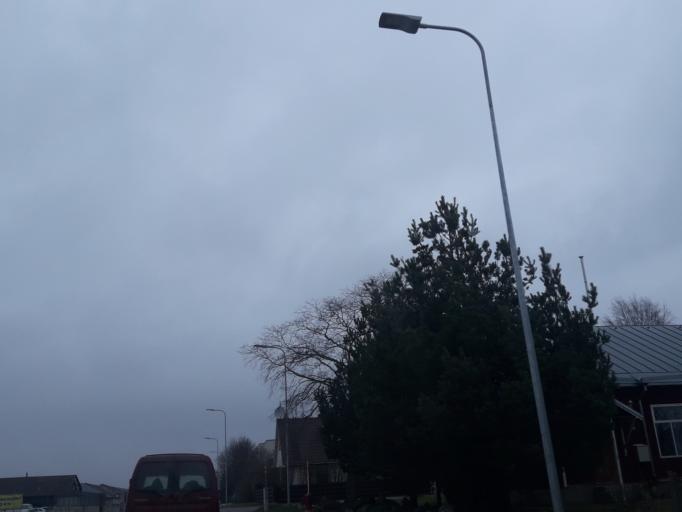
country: EE
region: Saare
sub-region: Kuressaare linn
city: Kuressaare
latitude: 58.2562
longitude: 22.4781
